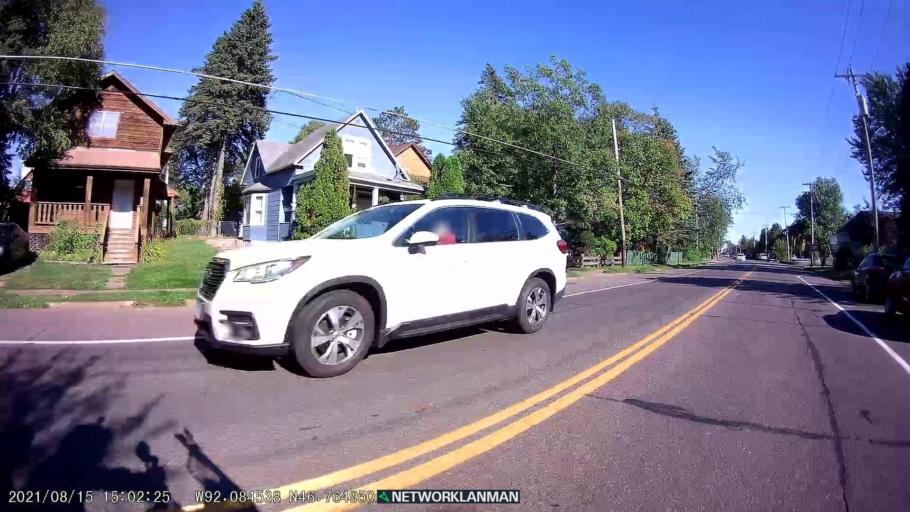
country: US
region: Minnesota
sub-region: Saint Louis County
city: Duluth
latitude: 46.7648
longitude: -92.0845
